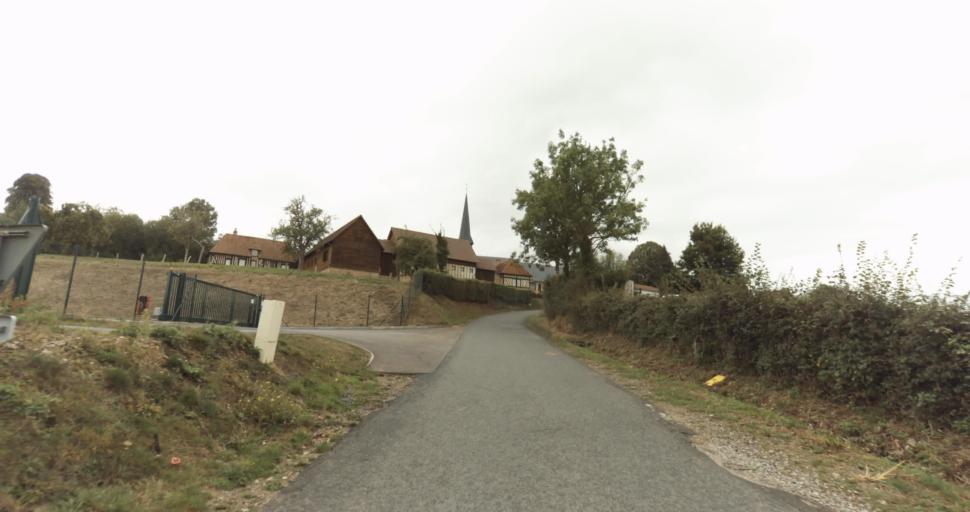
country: FR
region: Lower Normandy
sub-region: Departement de l'Orne
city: Vimoutiers
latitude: 48.8924
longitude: 0.1780
